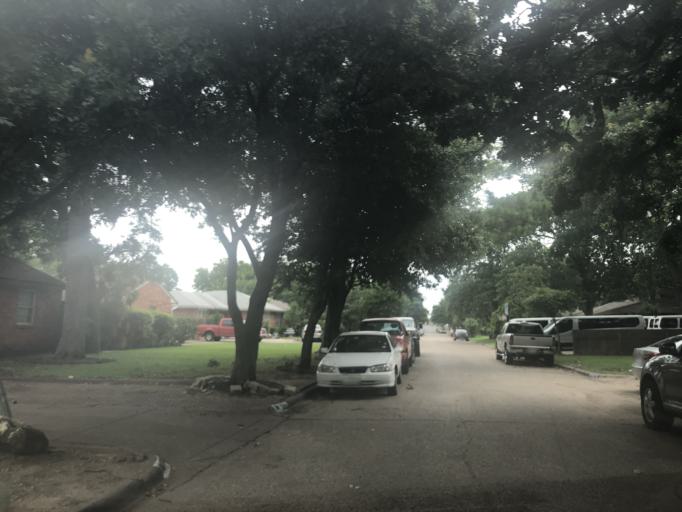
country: US
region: Texas
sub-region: Dallas County
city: University Park
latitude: 32.8574
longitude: -96.8685
